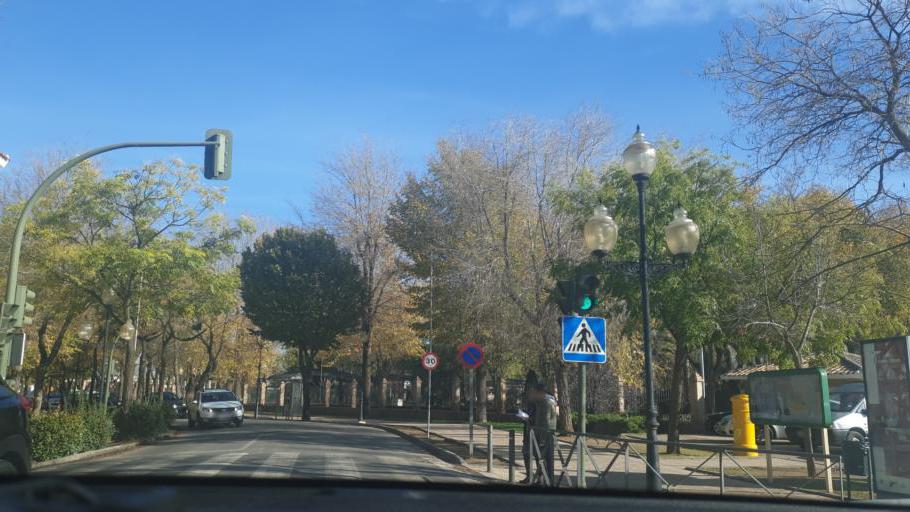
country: ES
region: Castille-La Mancha
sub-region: Provincia de Ciudad Real
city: Tomelloso
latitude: 39.1481
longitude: -3.0235
